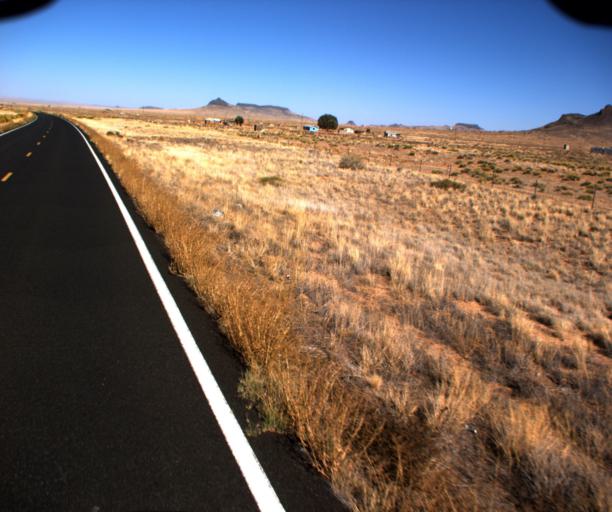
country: US
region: Arizona
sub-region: Navajo County
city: Dilkon
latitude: 35.4674
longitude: -110.4228
